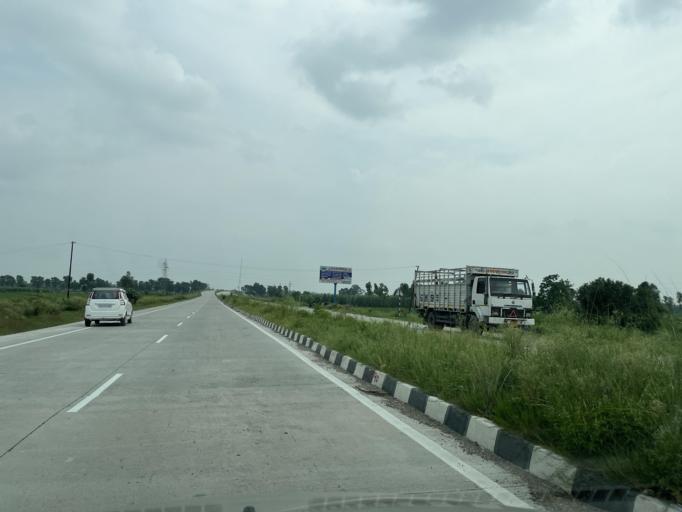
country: IN
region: Uttarakhand
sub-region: Udham Singh Nagar
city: Kashipur
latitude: 29.1957
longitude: 78.9360
